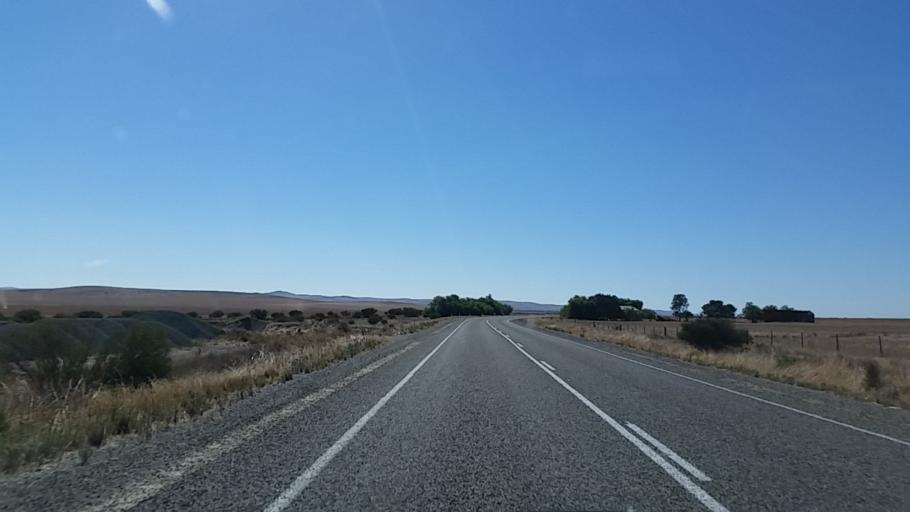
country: AU
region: South Australia
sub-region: Northern Areas
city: Jamestown
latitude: -33.2846
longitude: 138.8695
